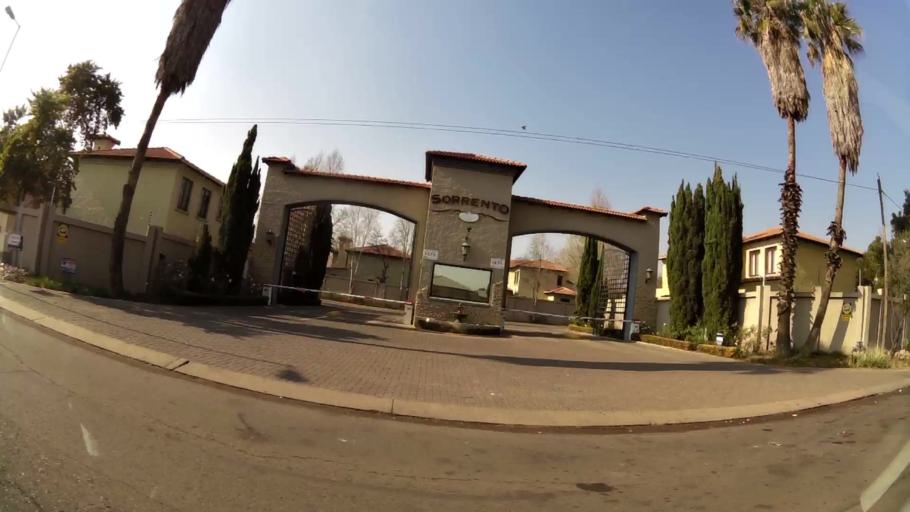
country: ZA
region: Gauteng
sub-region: City of Tshwane Metropolitan Municipality
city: Pretoria
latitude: -25.7650
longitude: 28.3417
